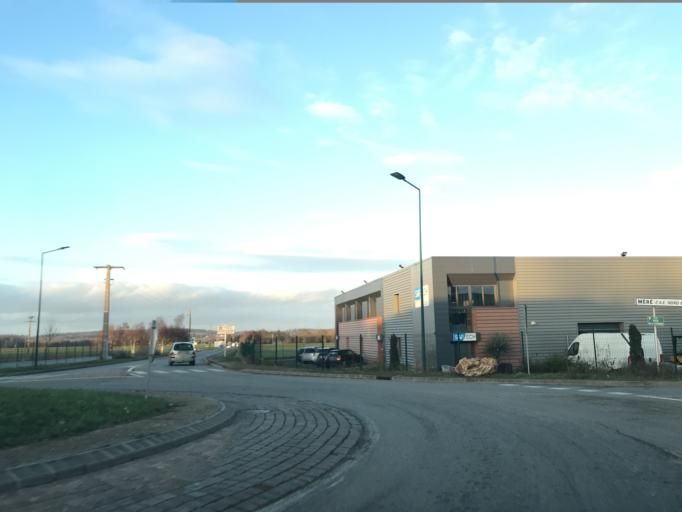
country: FR
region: Ile-de-France
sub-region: Departement des Yvelines
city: Mere
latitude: 48.8050
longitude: 1.8161
